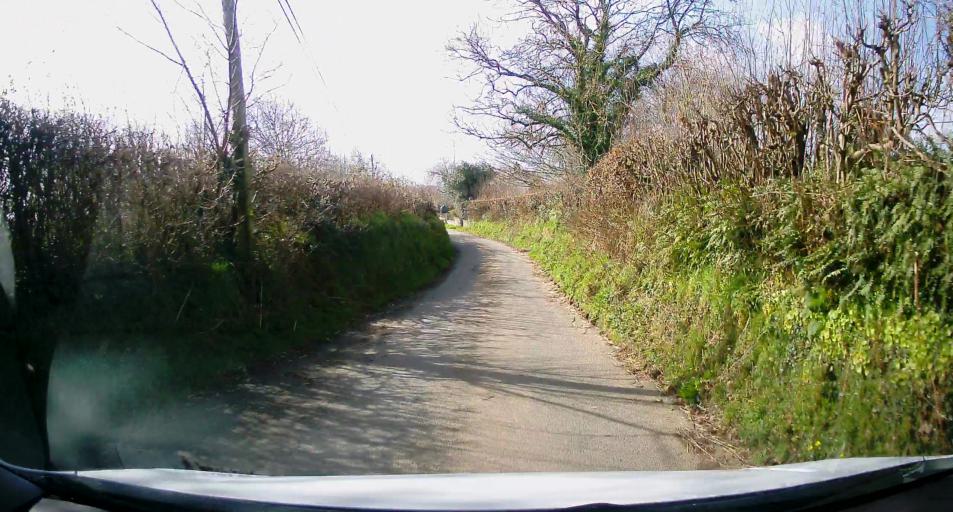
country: GB
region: Wales
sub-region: County of Ceredigion
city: Aberporth
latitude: 52.0692
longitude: -4.5665
